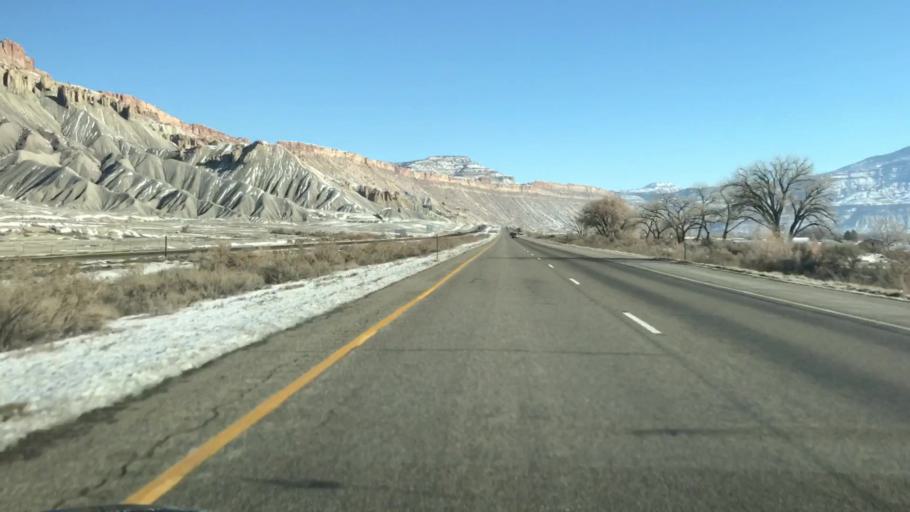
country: US
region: Colorado
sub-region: Mesa County
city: Clifton
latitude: 39.1095
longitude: -108.4217
